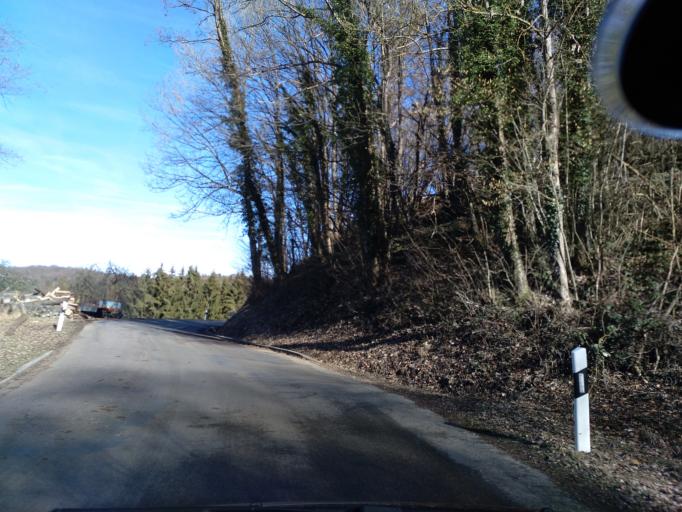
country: DE
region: Baden-Wuerttemberg
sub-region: Regierungsbezirk Stuttgart
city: Mainhardt
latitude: 49.0840
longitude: 9.5611
